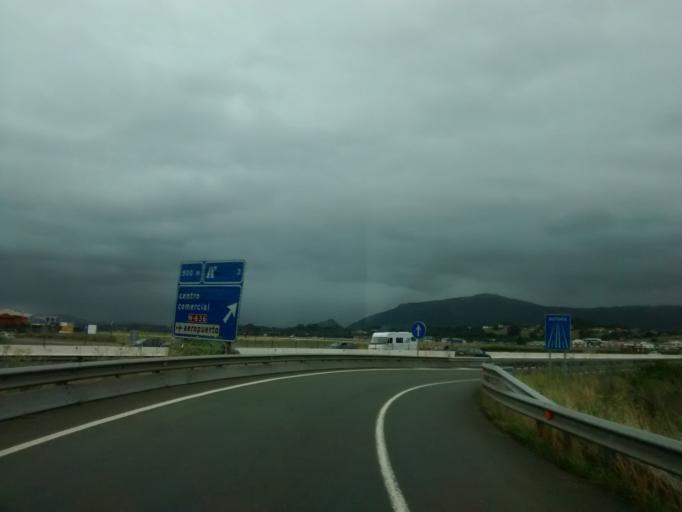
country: ES
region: Cantabria
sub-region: Provincia de Cantabria
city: El Astillero
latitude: 43.4330
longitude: -3.8376
